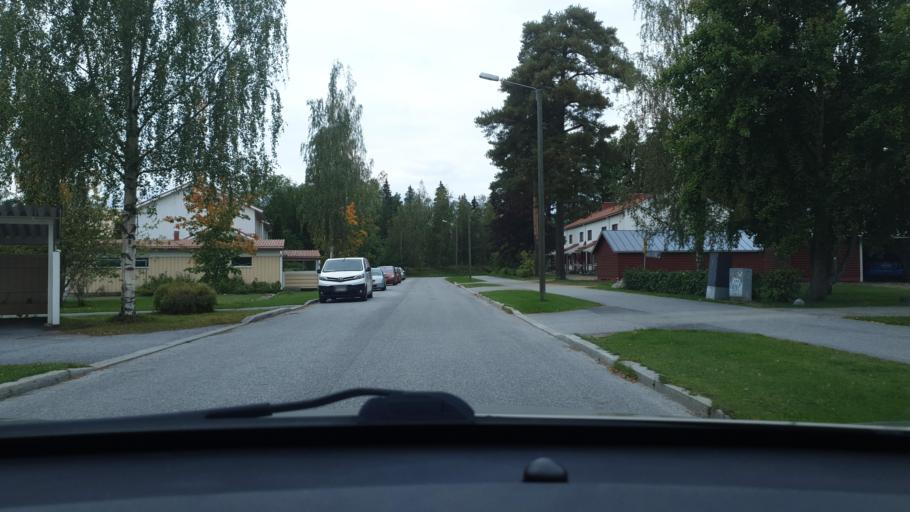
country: FI
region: Ostrobothnia
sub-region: Vaasa
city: Teeriniemi
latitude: 63.0864
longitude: 21.6813
